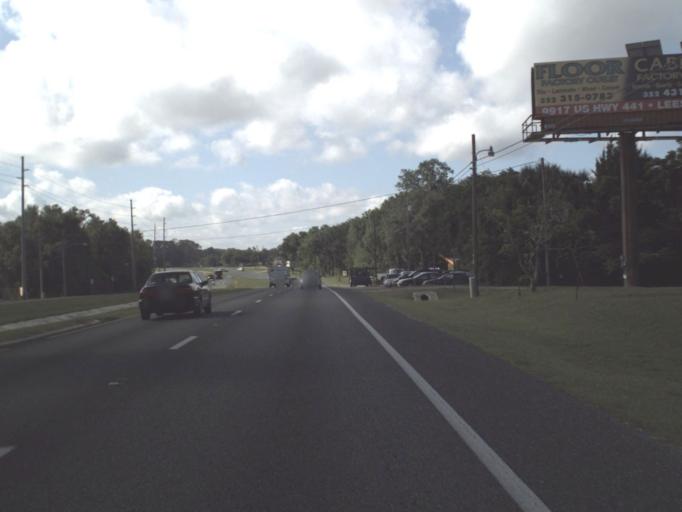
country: US
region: Florida
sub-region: Lake County
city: Lady Lake
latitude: 28.9050
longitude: -81.9156
